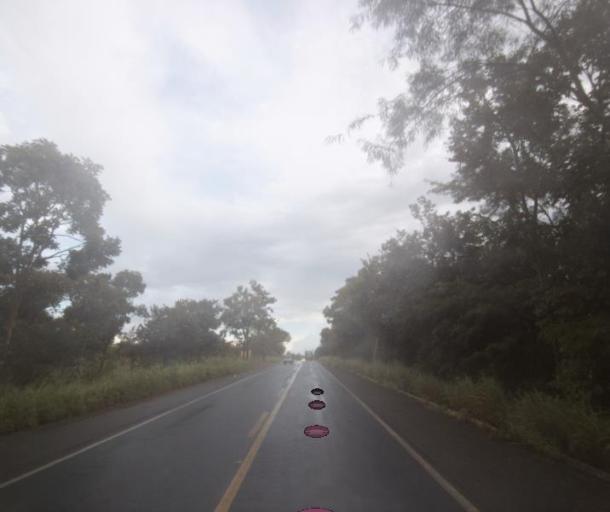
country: BR
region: Goias
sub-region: Porangatu
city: Porangatu
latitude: -13.8211
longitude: -49.0415
